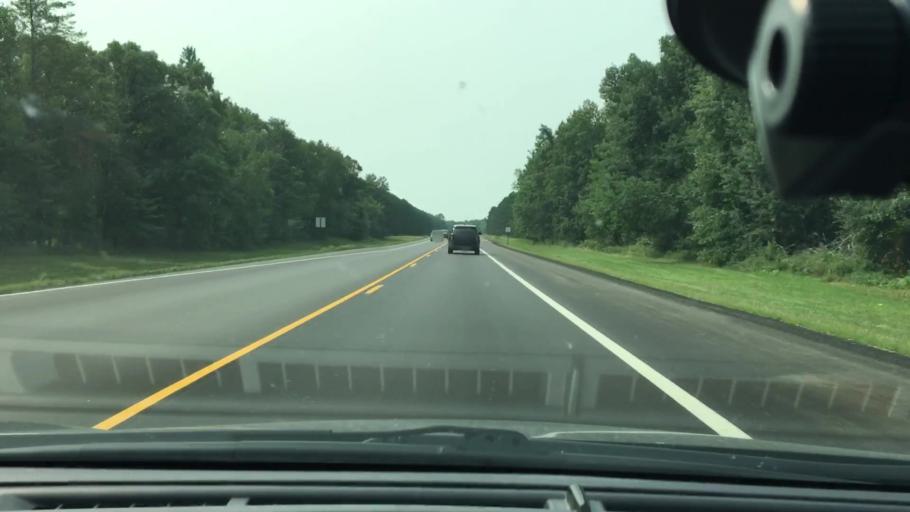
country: US
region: Minnesota
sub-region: Crow Wing County
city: Brainerd
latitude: 46.4338
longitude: -94.1730
